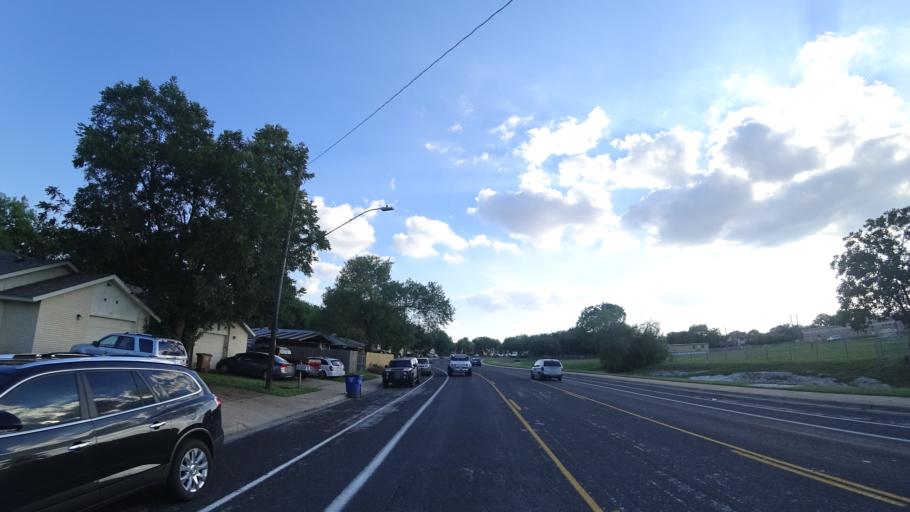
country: US
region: Texas
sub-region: Travis County
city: Wells Branch
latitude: 30.3649
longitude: -97.7078
